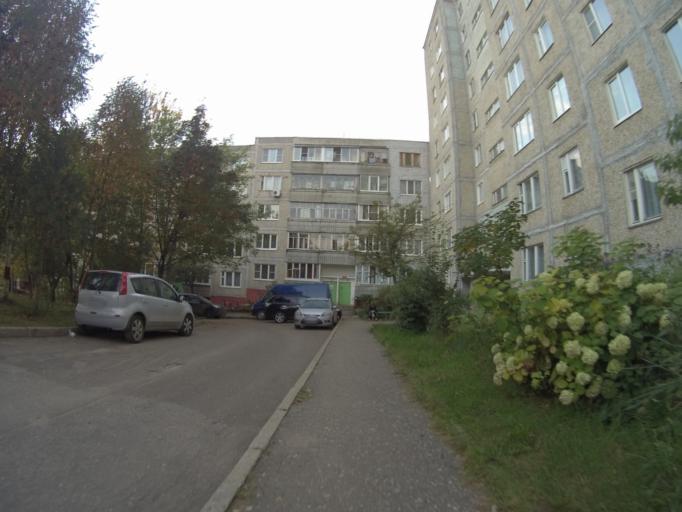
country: RU
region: Vladimir
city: Vladimir
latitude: 56.1049
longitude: 40.3516
